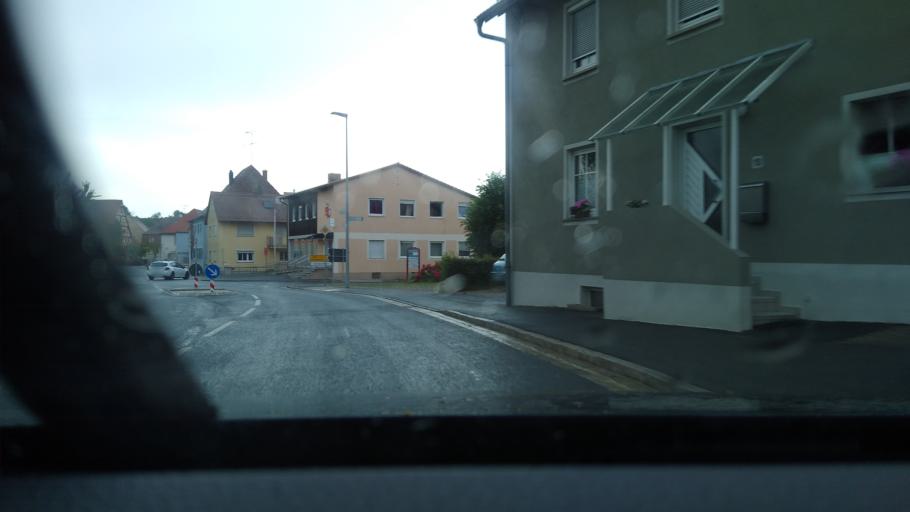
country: DE
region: Bavaria
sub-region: Regierungsbezirk Mittelfranken
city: Obernzenn
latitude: 49.4490
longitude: 10.4679
